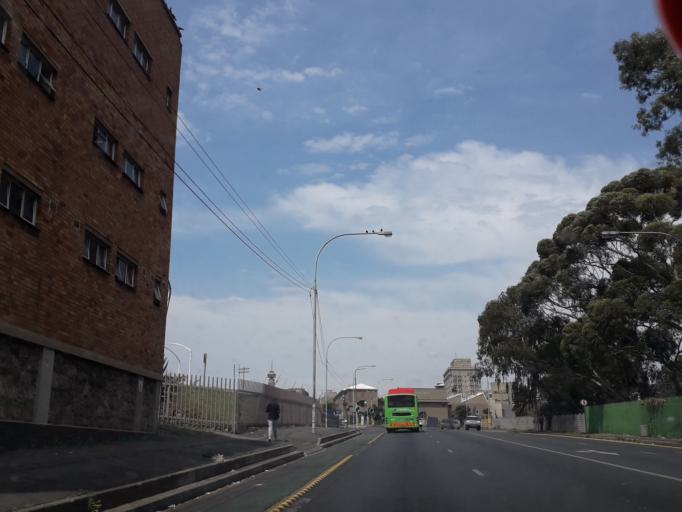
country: ZA
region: Gauteng
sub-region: City of Johannesburg Metropolitan Municipality
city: Johannesburg
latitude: -26.1932
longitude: 28.0254
